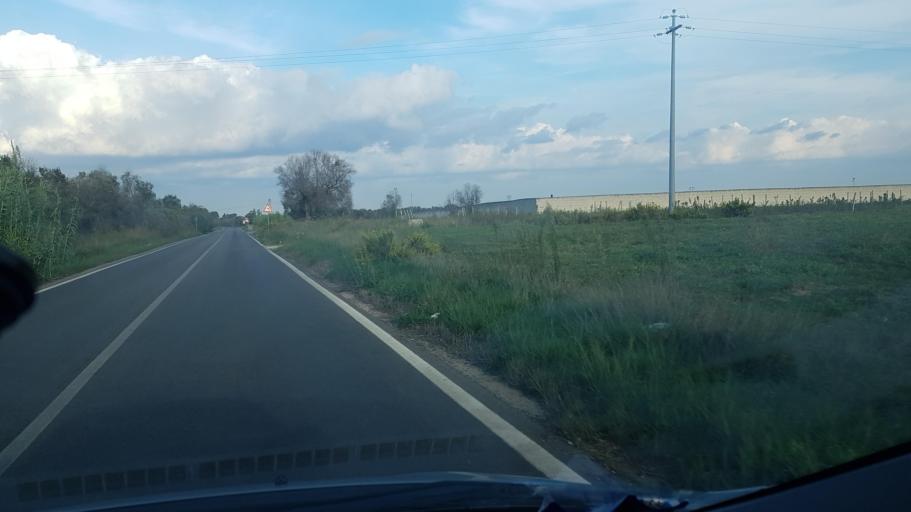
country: IT
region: Apulia
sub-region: Provincia di Lecce
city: Veglie
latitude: 40.3373
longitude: 17.9913
